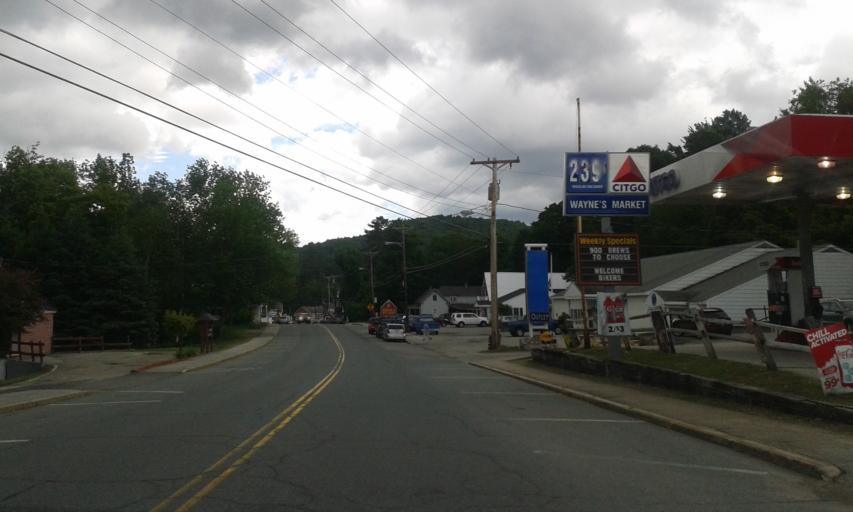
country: US
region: New Hampshire
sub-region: Grafton County
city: Woodstock
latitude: 44.0344
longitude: -71.6865
